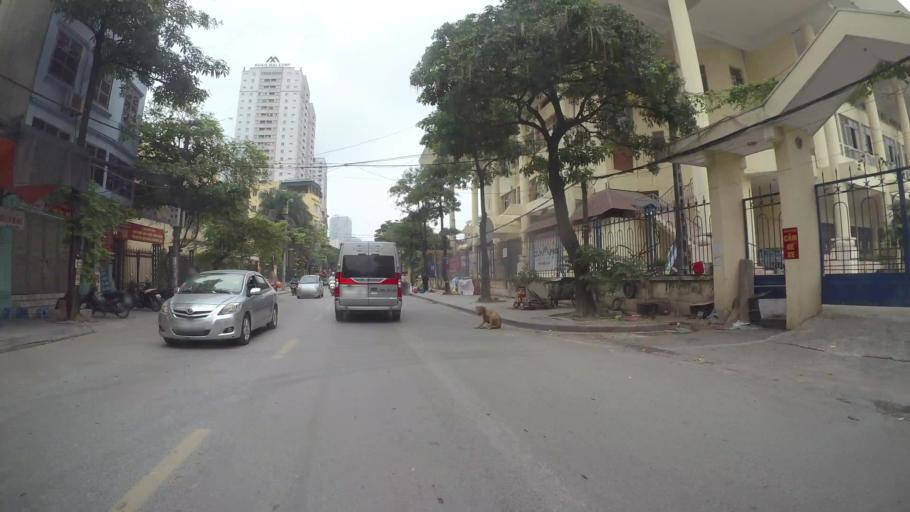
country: VN
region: Ha Noi
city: Ha Dong
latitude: 20.9674
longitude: 105.7703
